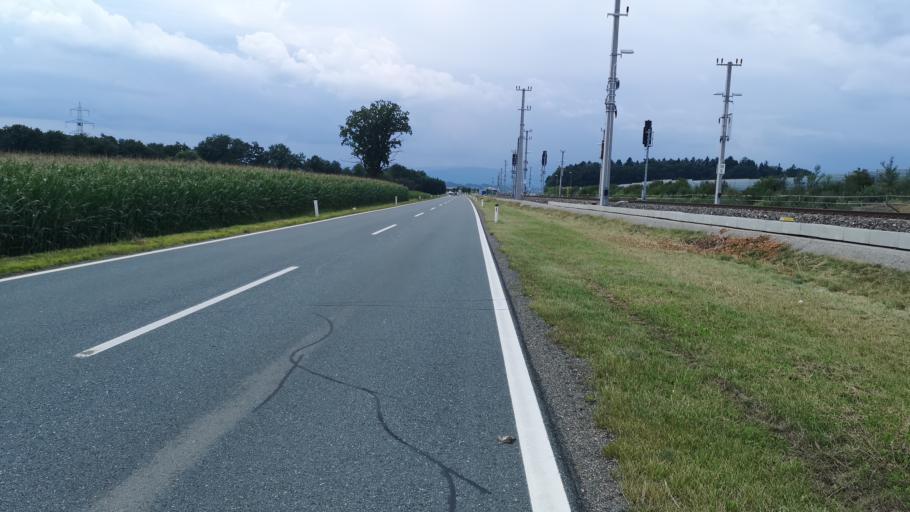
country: AT
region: Styria
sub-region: Politischer Bezirk Deutschlandsberg
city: Wettmannstatten
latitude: 46.8403
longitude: 15.3898
